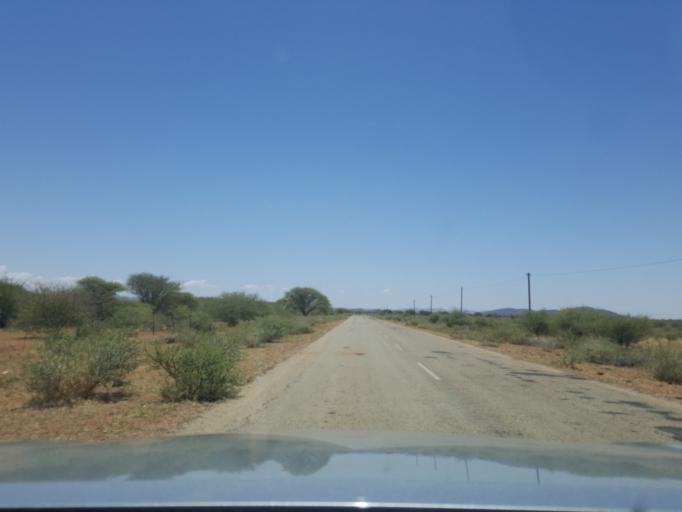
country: BW
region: South East
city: Ramotswa
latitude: -25.0138
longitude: 25.9065
